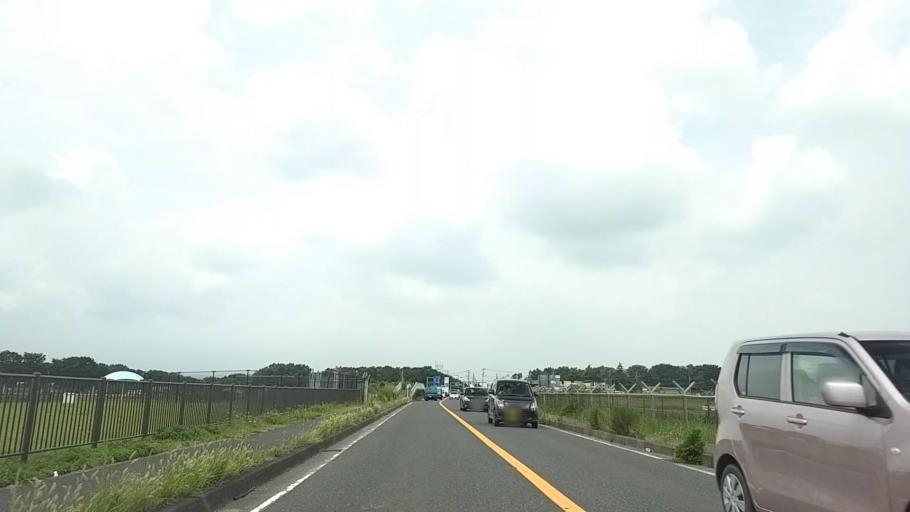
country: JP
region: Kanagawa
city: Minami-rinkan
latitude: 35.4398
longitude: 139.4510
